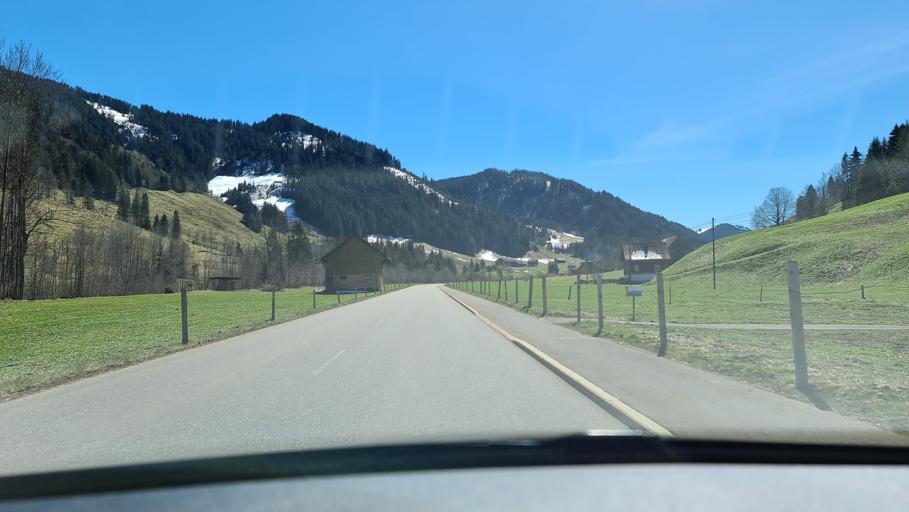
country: CH
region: Schwyz
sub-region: Bezirk Schwyz
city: Rothenthurm
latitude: 47.0831
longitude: 8.7226
